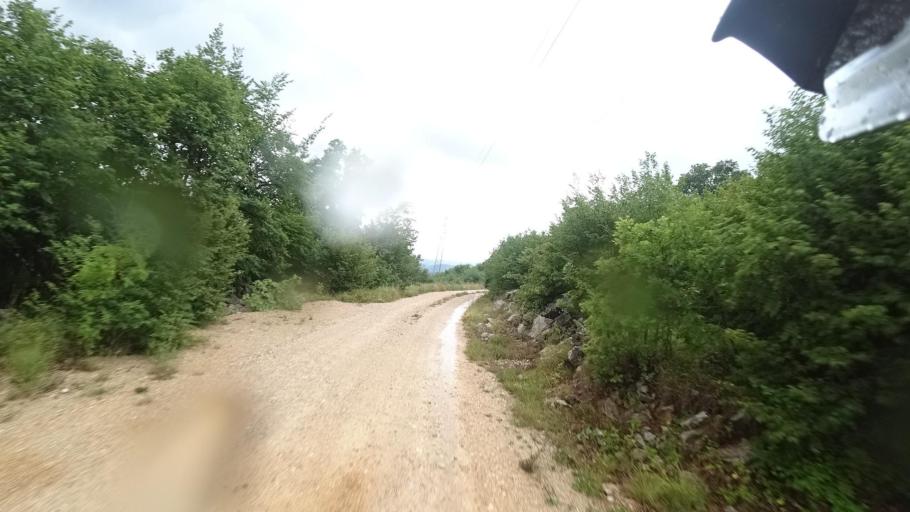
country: HR
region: Licko-Senjska
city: Jezerce
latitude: 44.7065
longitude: 15.6637
